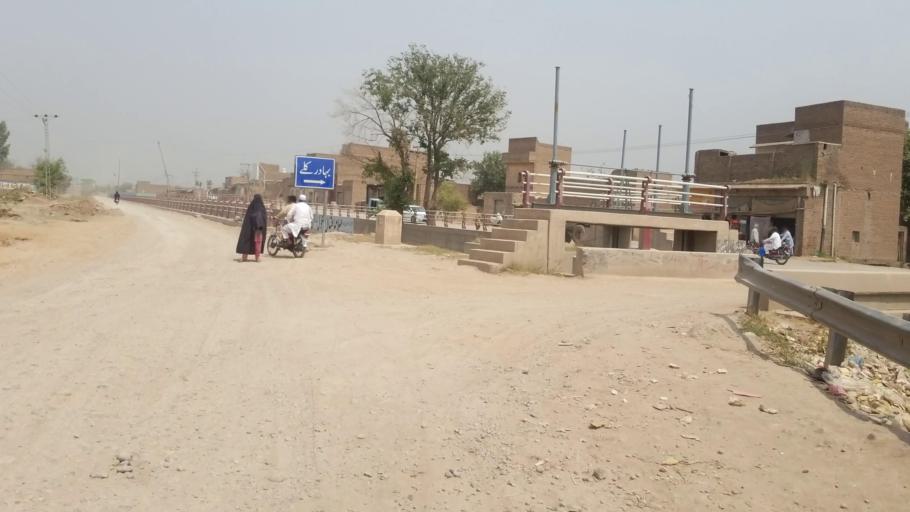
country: PK
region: Khyber Pakhtunkhwa
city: Peshawar
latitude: 33.9637
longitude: 71.5420
